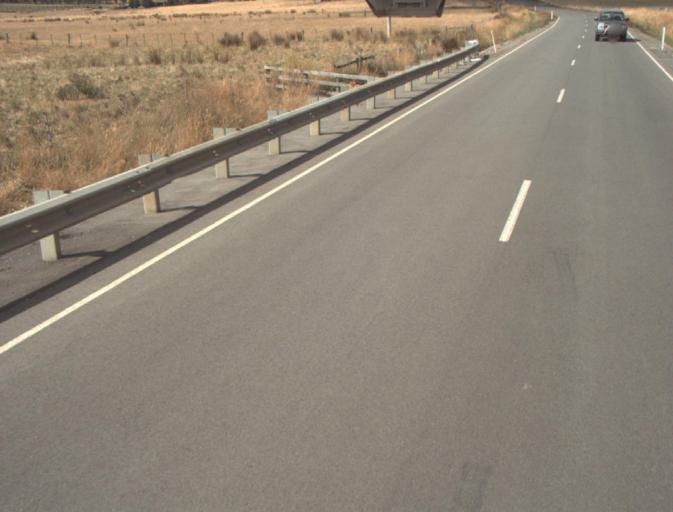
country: AU
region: Tasmania
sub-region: Launceston
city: Mayfield
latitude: -41.2204
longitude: 147.1374
